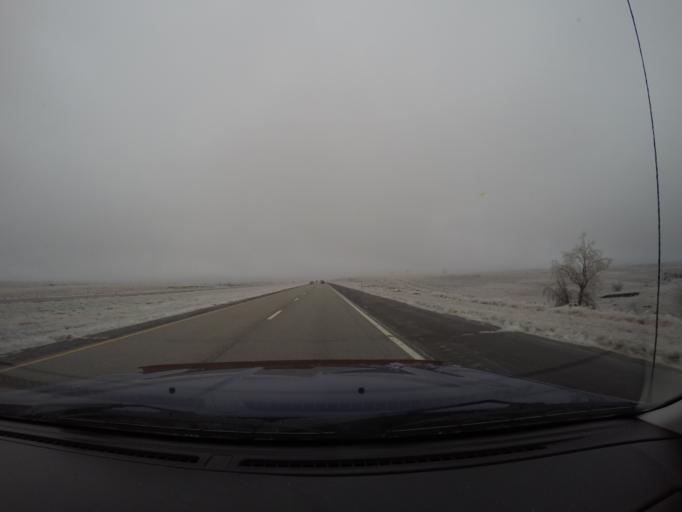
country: US
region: Kansas
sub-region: Riley County
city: Manhattan
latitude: 39.0994
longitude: -96.5381
